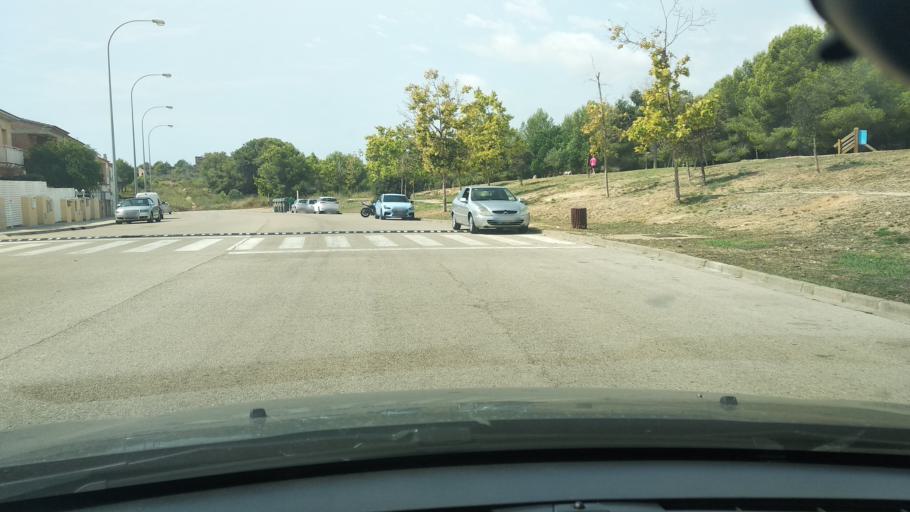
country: ES
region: Catalonia
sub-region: Provincia de Tarragona
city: El Vendrell
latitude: 41.2215
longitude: 1.5194
